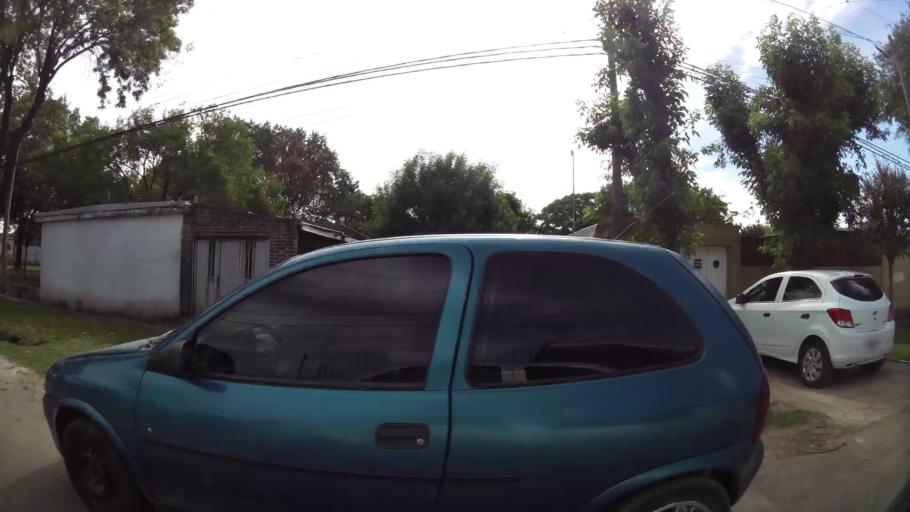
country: AR
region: Santa Fe
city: Granadero Baigorria
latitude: -32.9144
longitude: -60.7196
